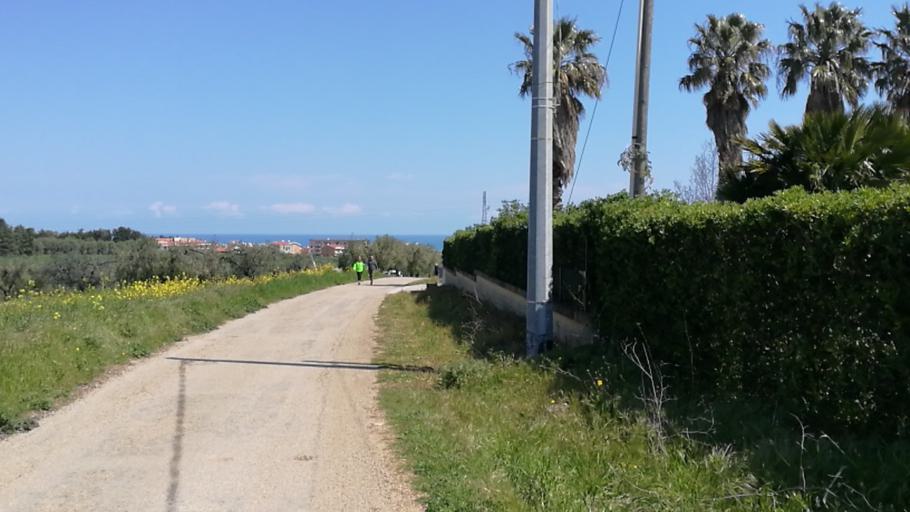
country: IT
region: Molise
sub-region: Provincia di Campobasso
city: Termoli
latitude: 41.9735
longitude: 14.9830
